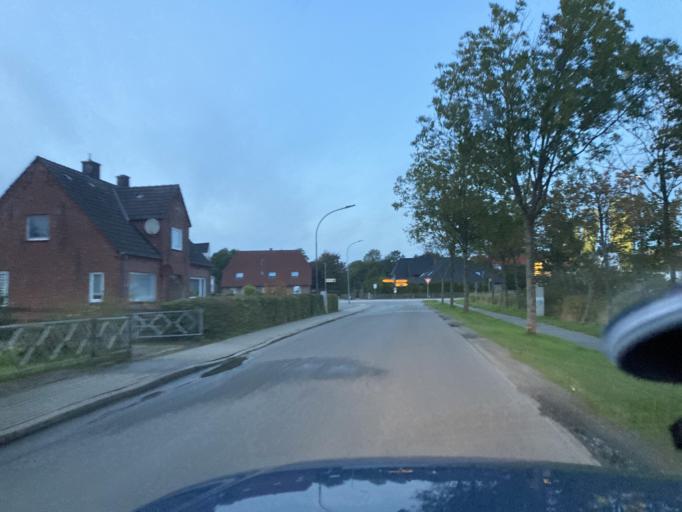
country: DE
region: Schleswig-Holstein
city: Garding
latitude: 54.3269
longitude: 8.7774
